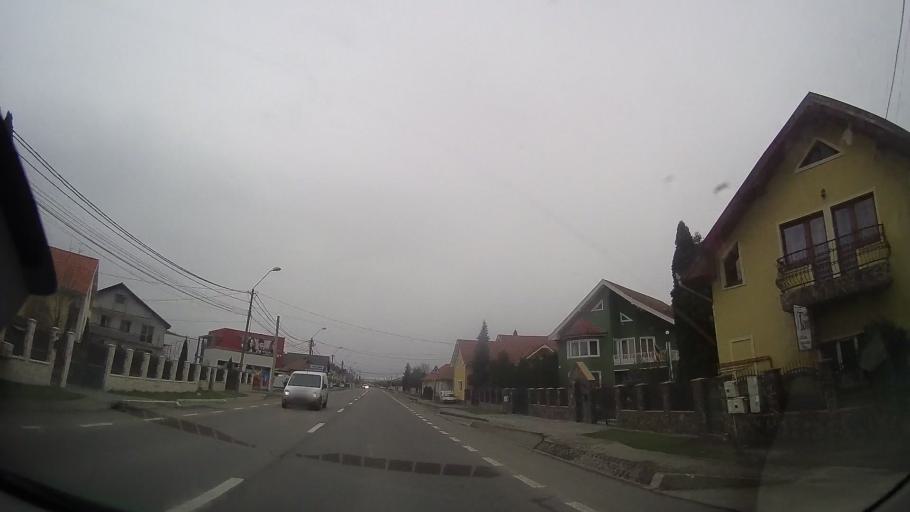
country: RO
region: Mures
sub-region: Comuna Santana de Mures
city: Santana de Mures
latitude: 46.5873
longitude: 24.5370
